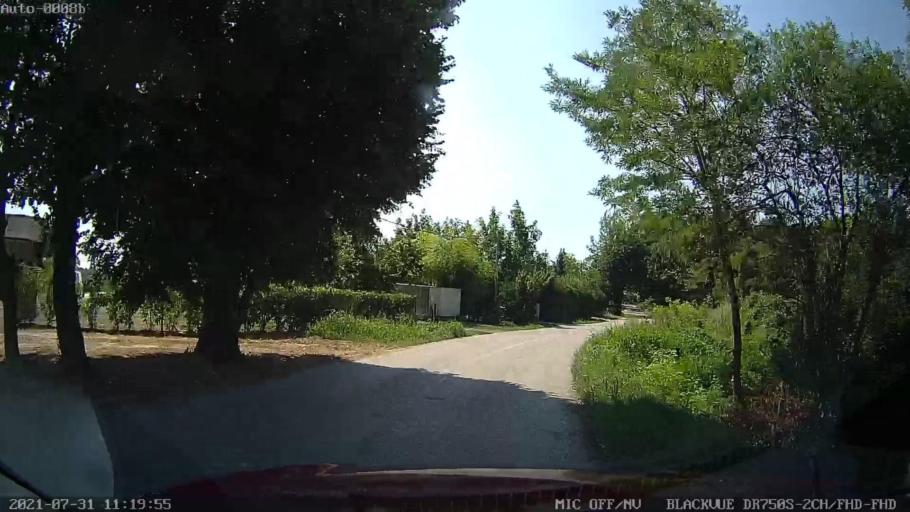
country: HR
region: Varazdinska
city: Jalzabet
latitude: 46.2365
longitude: 16.4763
